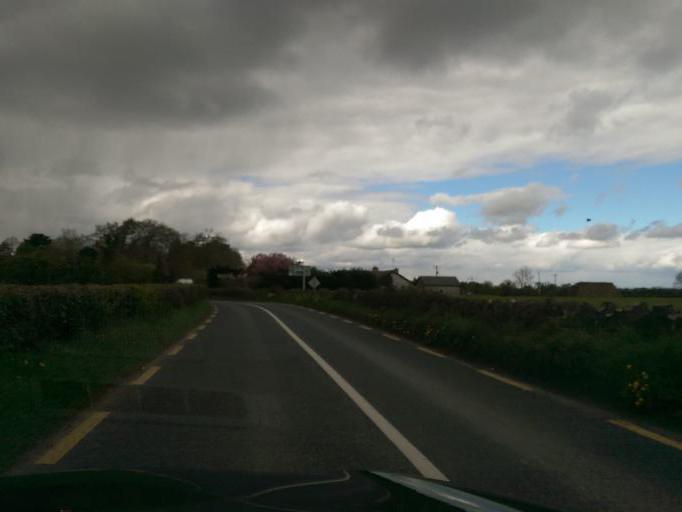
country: IE
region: Leinster
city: Lucan
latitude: 53.3733
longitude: -6.4569
